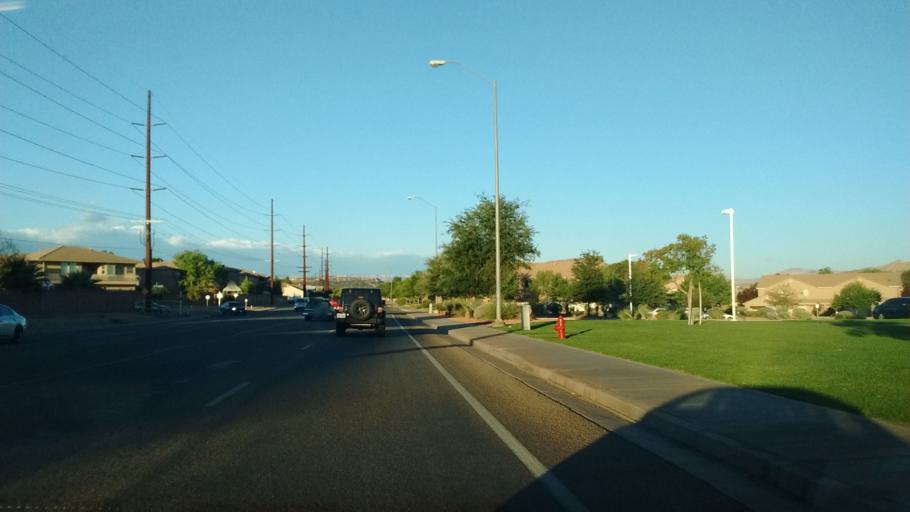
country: US
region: Utah
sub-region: Washington County
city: Washington
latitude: 37.1037
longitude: -113.5313
